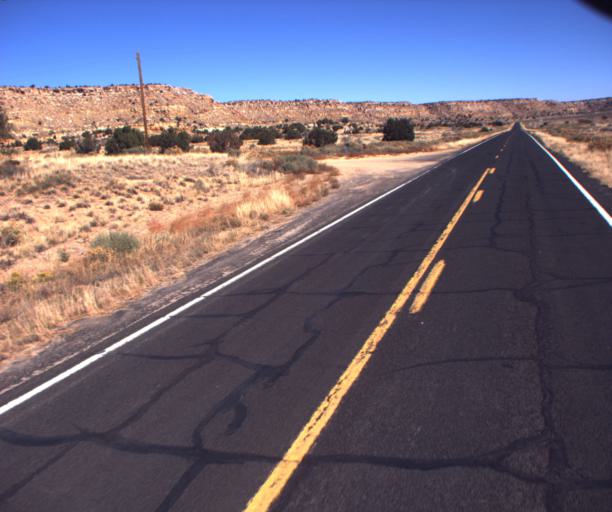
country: US
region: Arizona
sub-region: Navajo County
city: First Mesa
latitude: 35.8328
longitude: -110.2697
